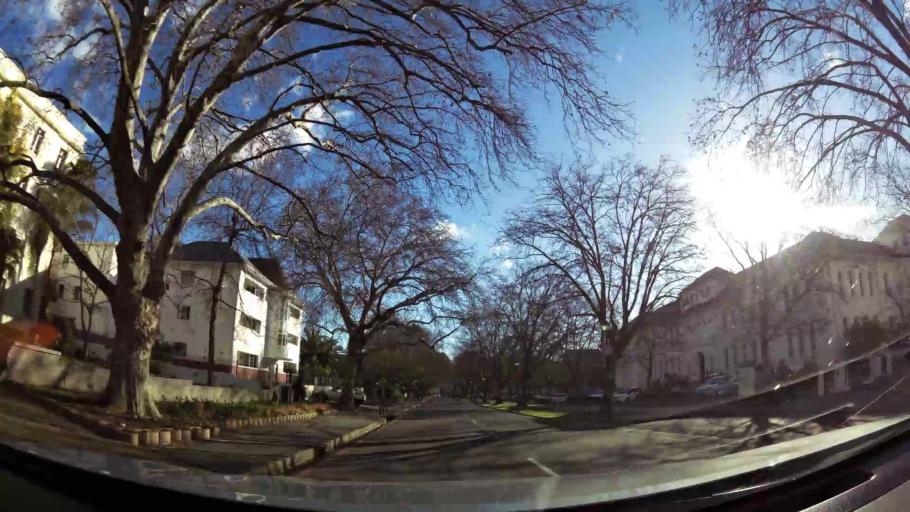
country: ZA
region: Western Cape
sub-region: Cape Winelands District Municipality
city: Stellenbosch
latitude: -33.9340
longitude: 18.8652
